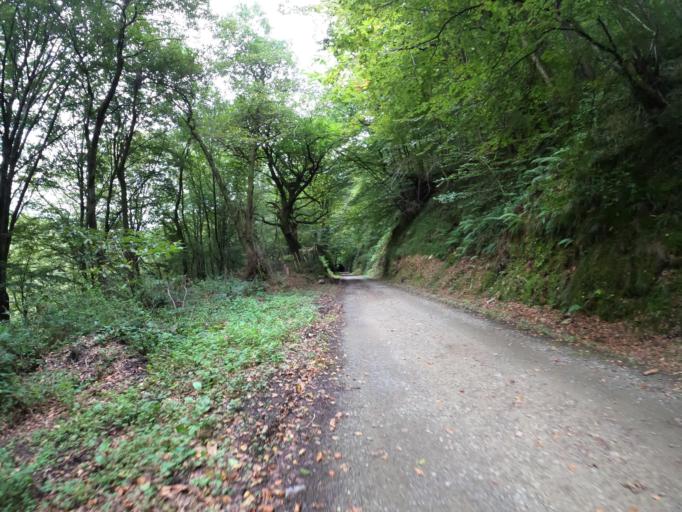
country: ES
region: Navarre
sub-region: Provincia de Navarra
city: Leitza
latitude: 43.0553
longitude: -1.9009
